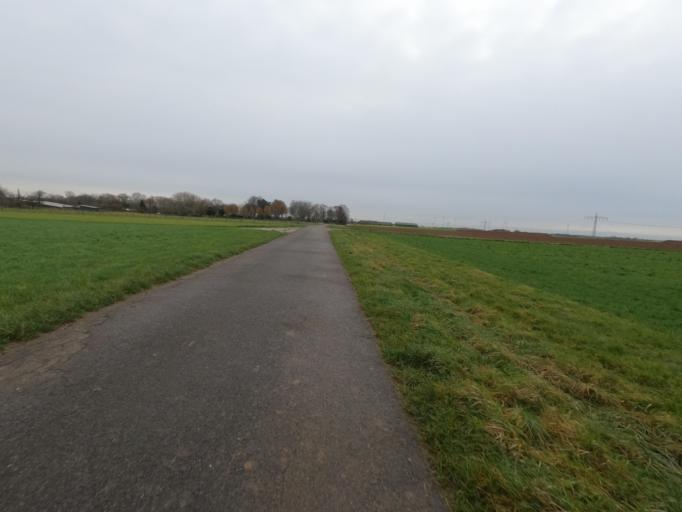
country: DE
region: North Rhine-Westphalia
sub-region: Regierungsbezirk Koln
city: Heinsberg
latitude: 51.0467
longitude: 6.1203
